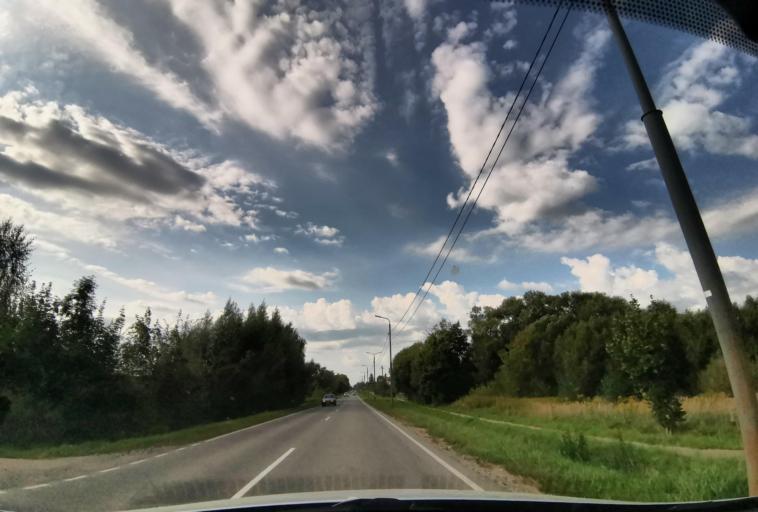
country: RU
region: Kaliningrad
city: Neman
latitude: 55.0213
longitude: 22.0725
